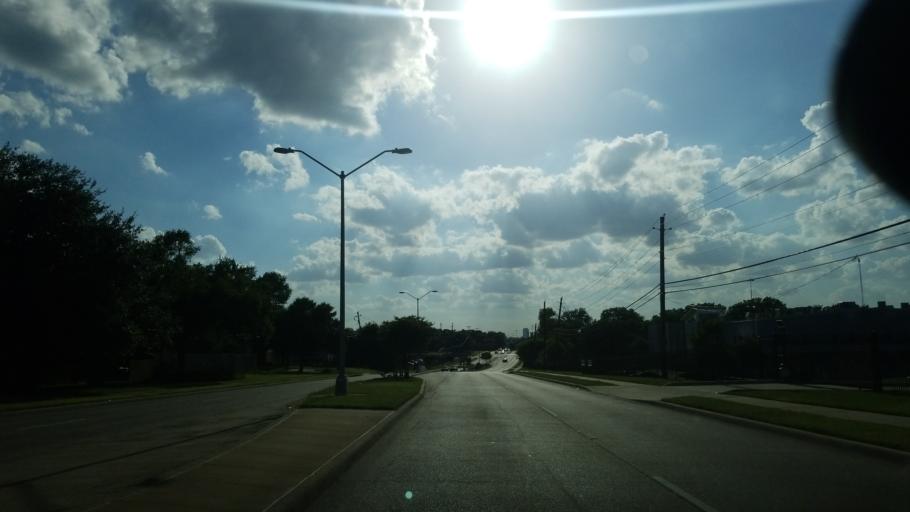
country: US
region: Texas
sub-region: Dallas County
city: Highland Park
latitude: 32.7923
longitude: -96.7087
